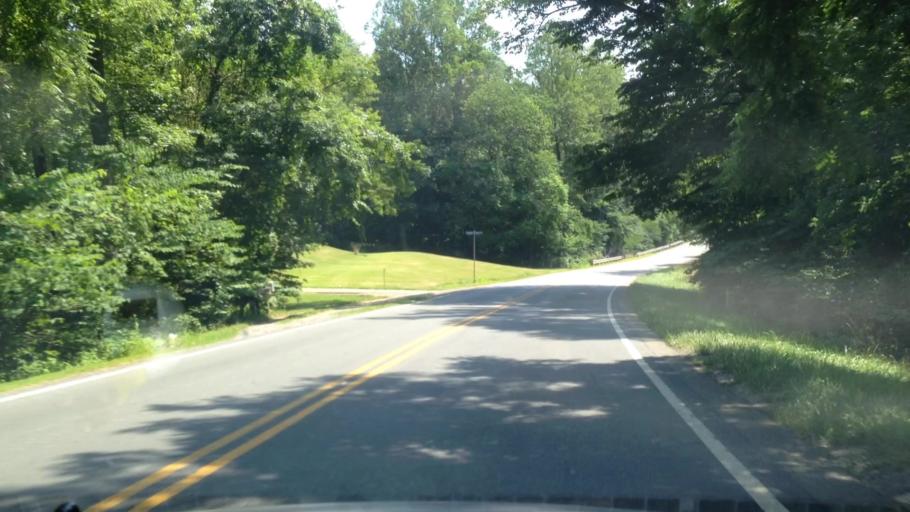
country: US
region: Virginia
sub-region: Patrick County
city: Stuart
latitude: 36.5941
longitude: -80.3149
